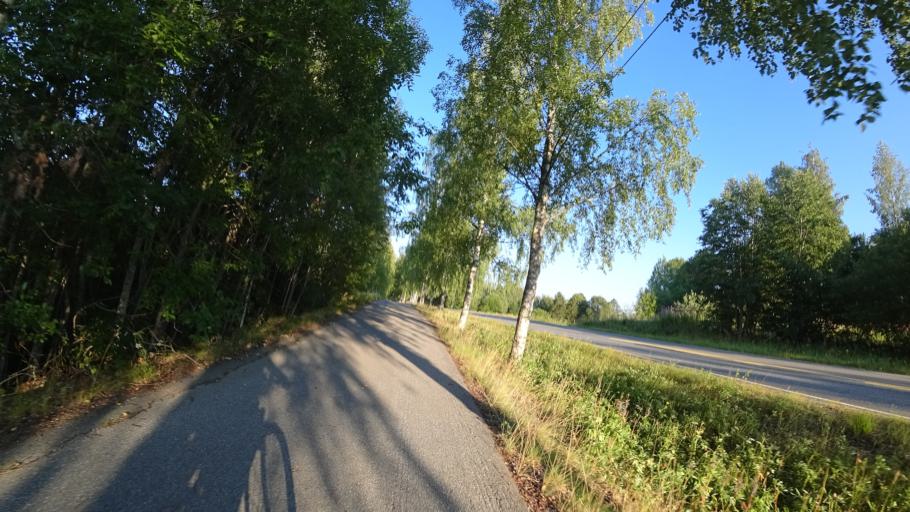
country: FI
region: Pirkanmaa
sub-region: Tampere
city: Nokia
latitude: 61.4720
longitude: 23.3832
